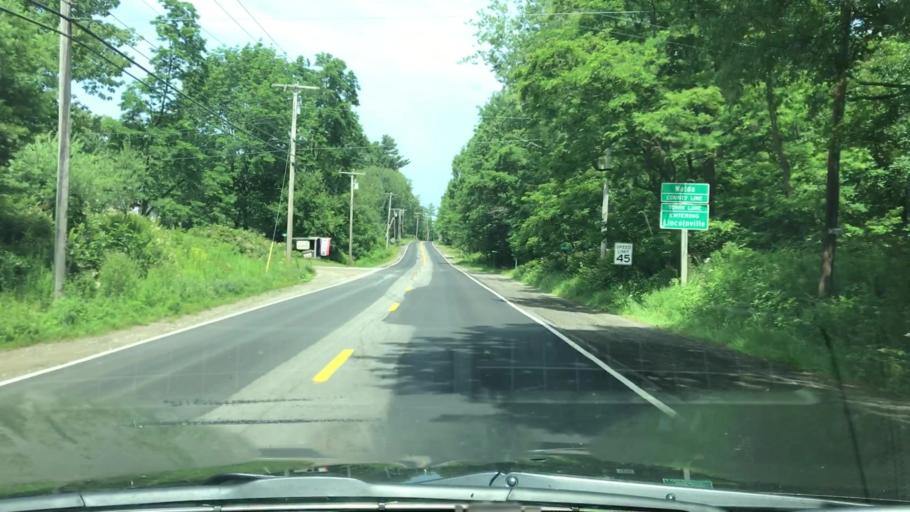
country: US
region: Maine
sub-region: Waldo County
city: Lincolnville
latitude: 44.2510
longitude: -69.0320
